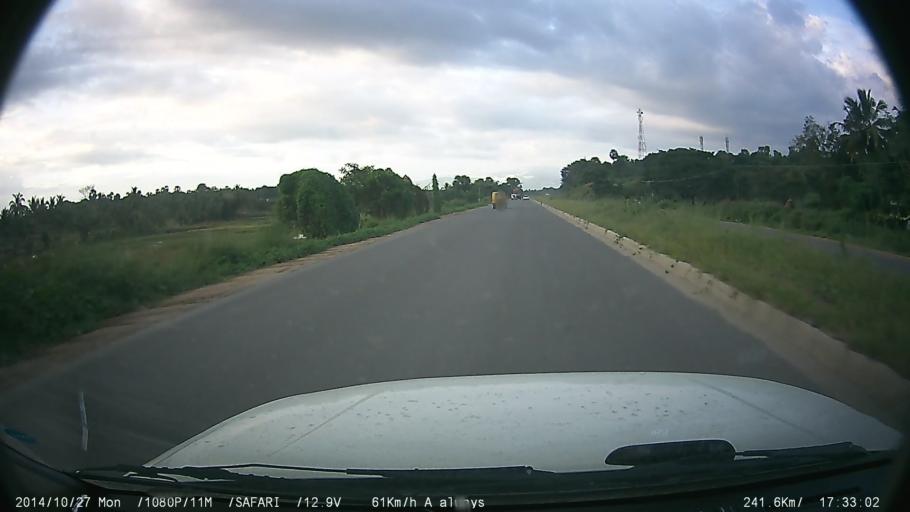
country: IN
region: Kerala
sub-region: Palakkad district
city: Palakkad
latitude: 10.6778
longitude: 76.5779
